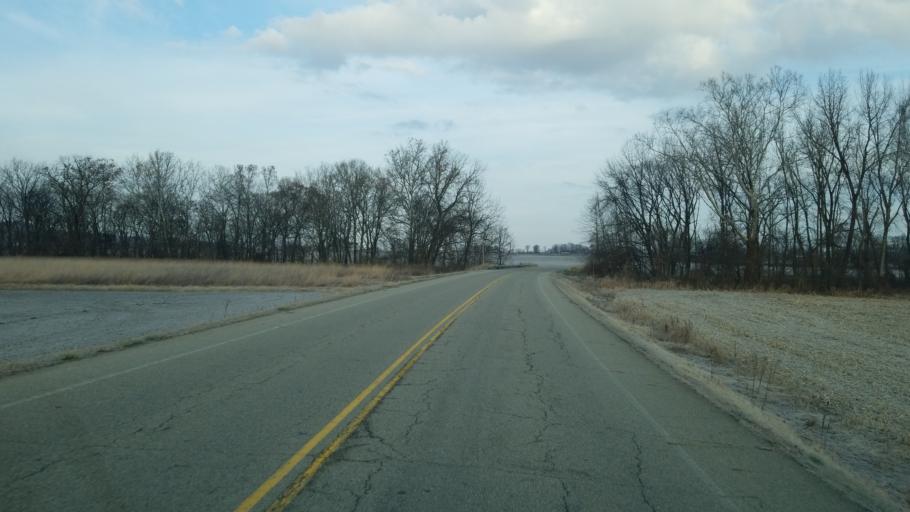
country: US
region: Ohio
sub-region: Ross County
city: Chillicothe
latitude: 39.2300
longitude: -82.8574
